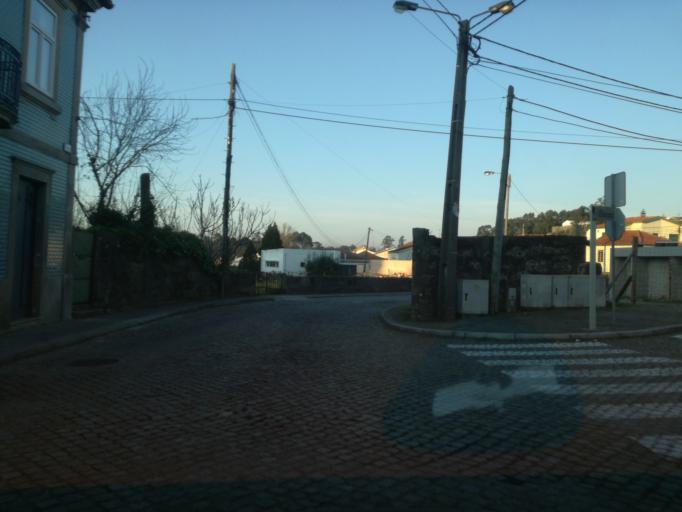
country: PT
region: Porto
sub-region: Maia
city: Milheiros
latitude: 41.2159
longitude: -8.5932
